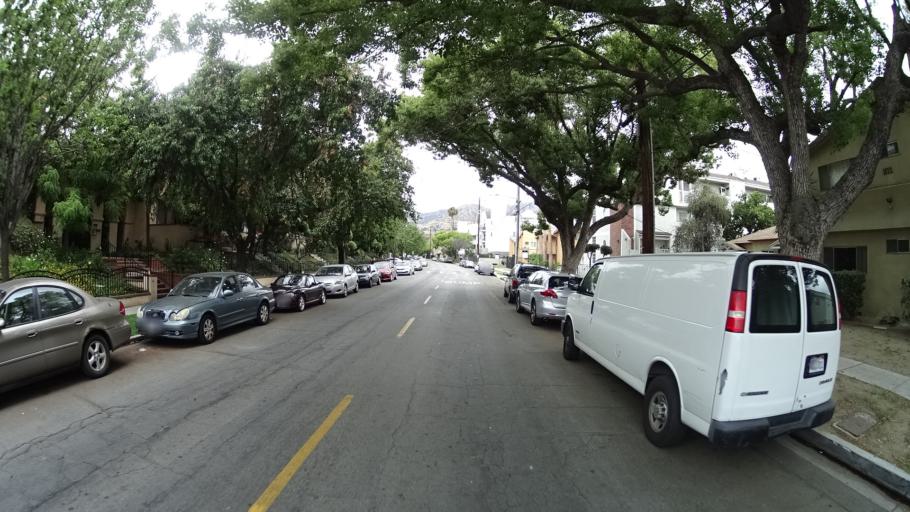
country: US
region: California
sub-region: Los Angeles County
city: Burbank
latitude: 34.1935
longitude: -118.3253
